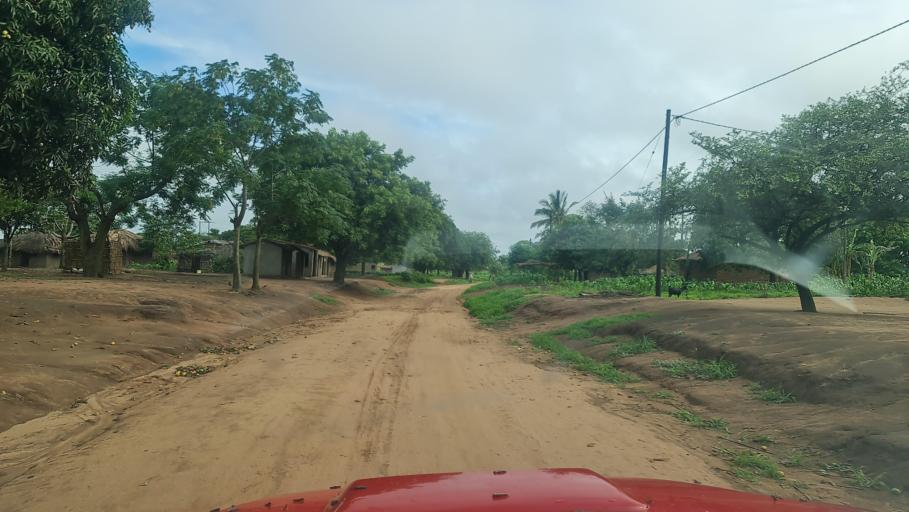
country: MW
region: Southern Region
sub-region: Nsanje District
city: Nsanje
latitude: -17.2965
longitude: 35.5939
